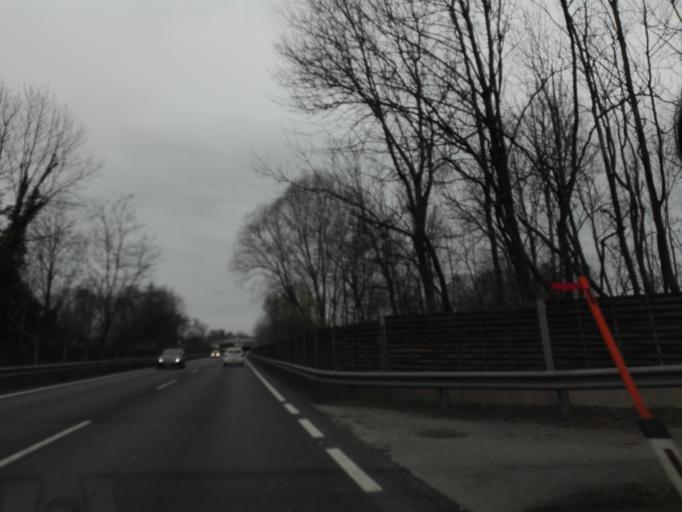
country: AT
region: Upper Austria
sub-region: Politischer Bezirk Linz-Land
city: Traun
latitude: 48.2158
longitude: 14.2340
